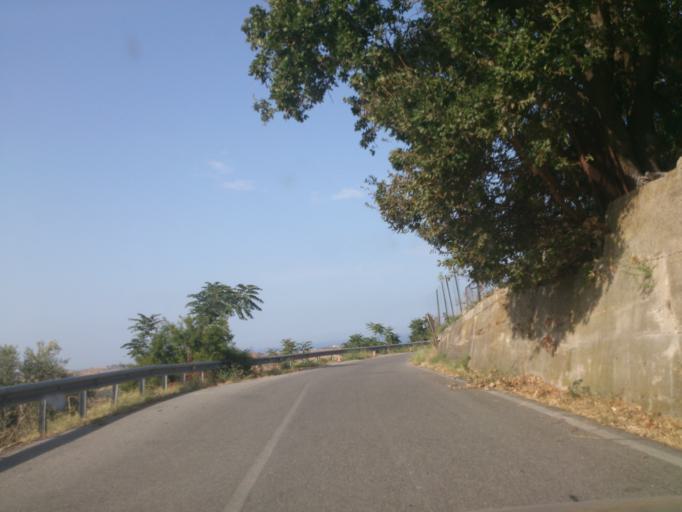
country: IT
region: Calabria
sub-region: Provincia di Reggio Calabria
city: Monasterace
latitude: 38.4520
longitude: 16.5480
